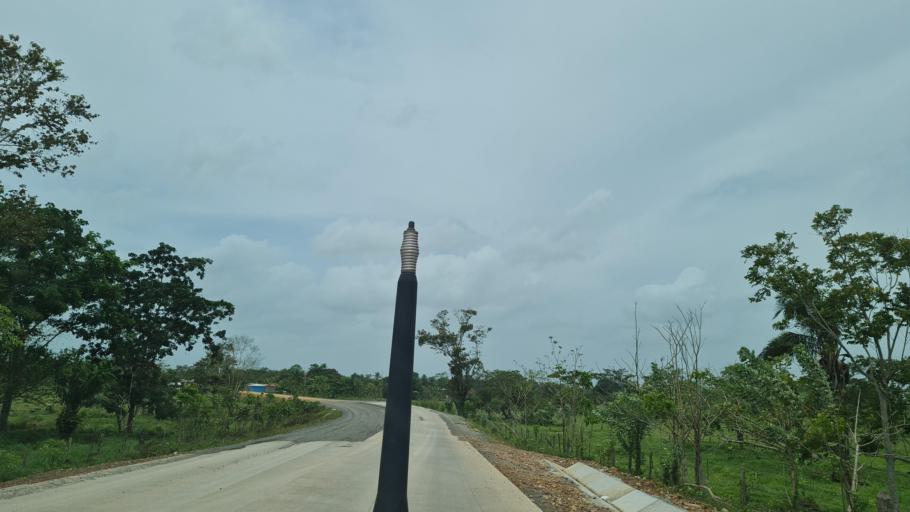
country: NI
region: Atlantico Norte (RAAN)
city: Bonanza
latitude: 14.0412
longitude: -84.0742
